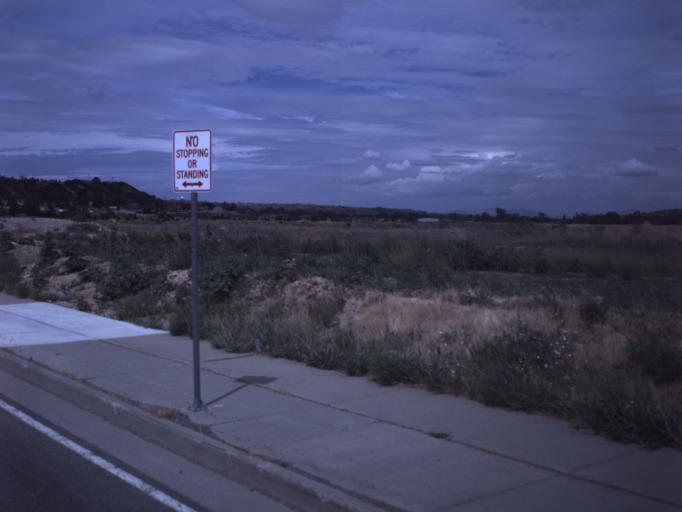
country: US
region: Utah
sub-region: Davis County
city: South Weber
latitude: 41.1273
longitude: -111.9130
